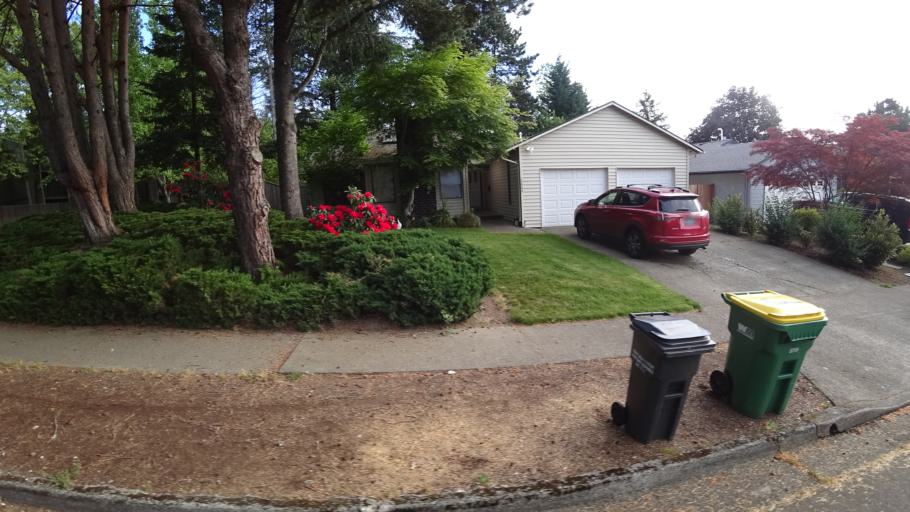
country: US
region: Oregon
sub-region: Washington County
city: Beaverton
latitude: 45.4752
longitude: -122.8213
